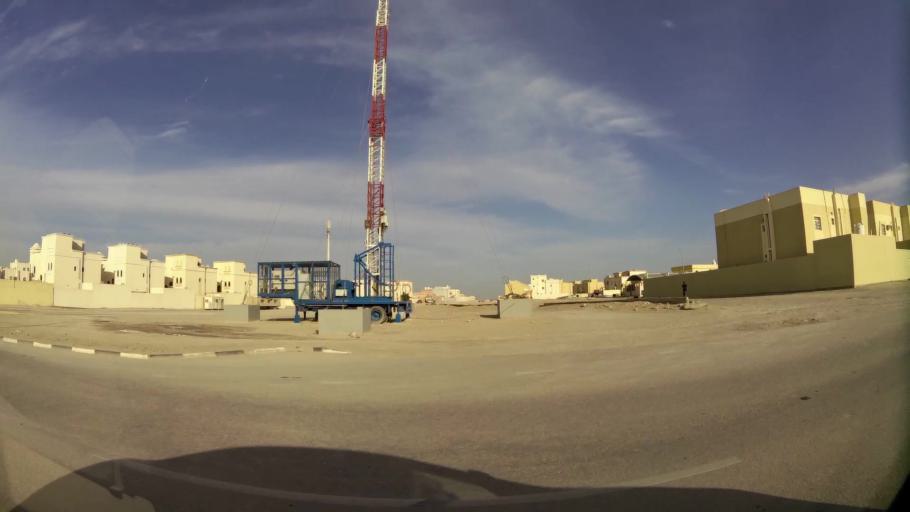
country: QA
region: Al Wakrah
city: Al Wakrah
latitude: 25.1487
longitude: 51.6061
